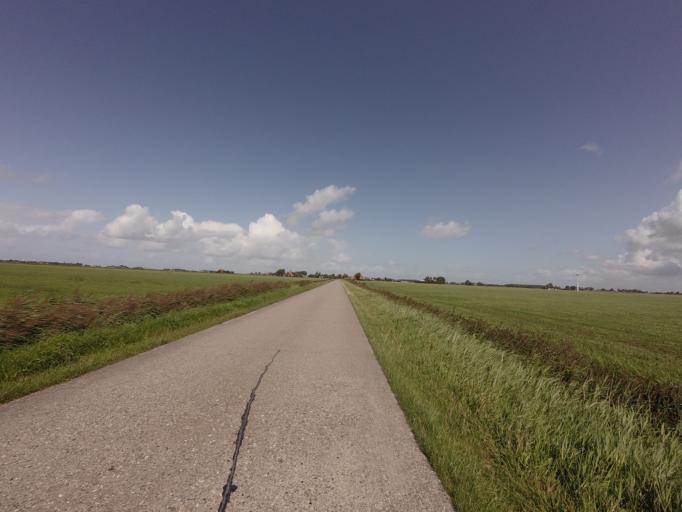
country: NL
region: Friesland
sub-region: Sudwest Fryslan
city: Makkum
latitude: 53.0711
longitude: 5.4540
